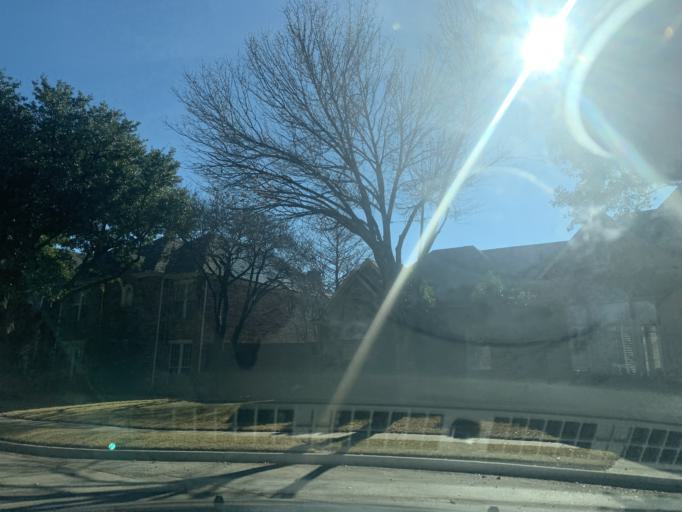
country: US
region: Texas
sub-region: Denton County
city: The Colony
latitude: 33.0521
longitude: -96.8160
